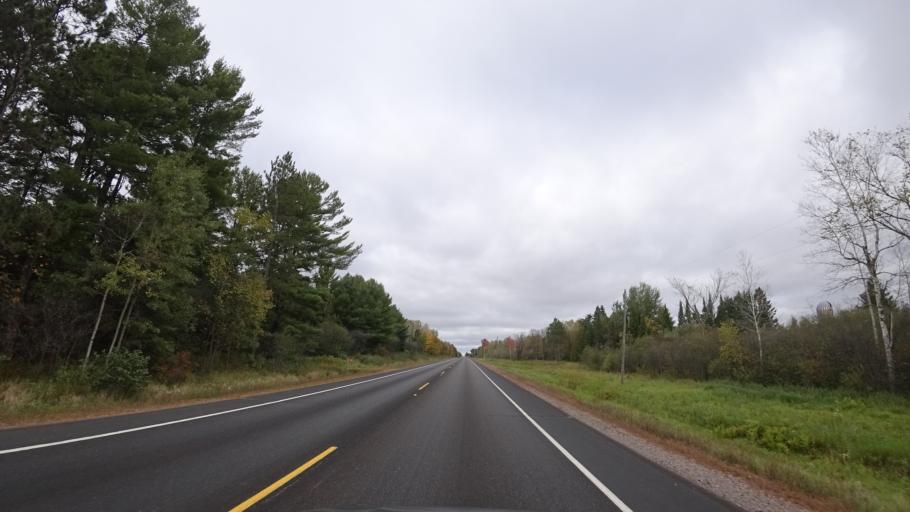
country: US
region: Wisconsin
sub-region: Rusk County
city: Ladysmith
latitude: 45.3480
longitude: -91.1109
